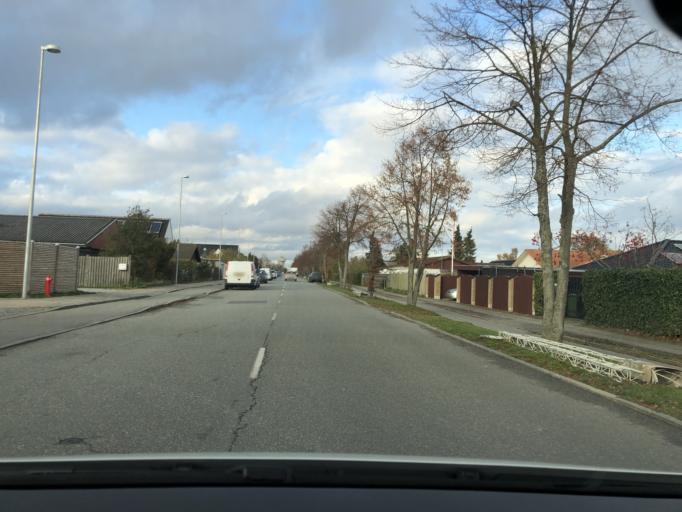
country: DK
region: Capital Region
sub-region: Tarnby Kommune
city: Tarnby
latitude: 55.6104
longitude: 12.5935
